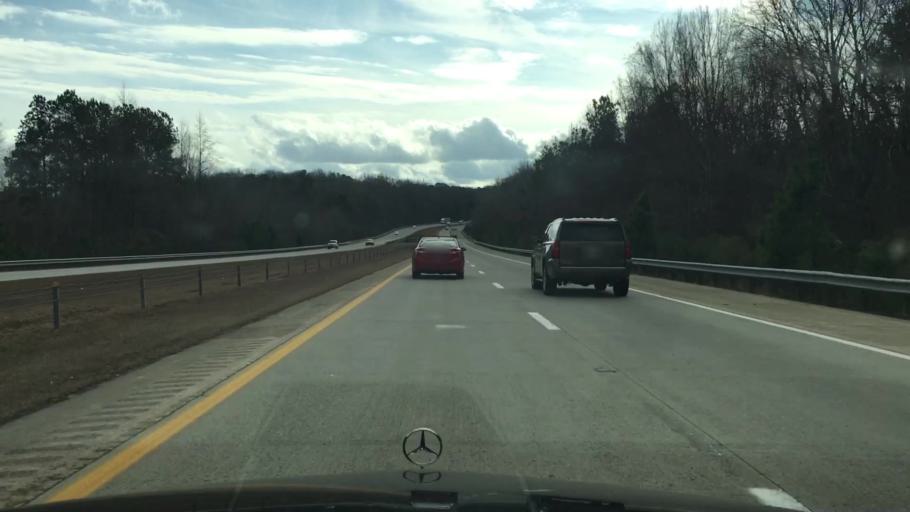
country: US
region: North Carolina
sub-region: Johnston County
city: Clayton
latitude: 35.5650
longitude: -78.5761
